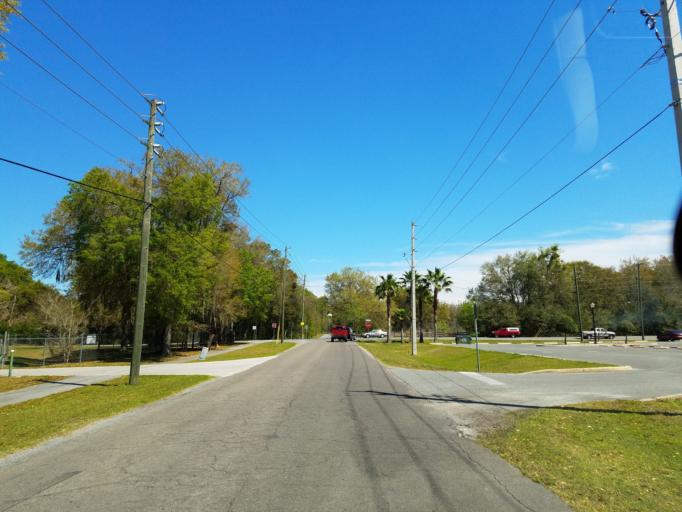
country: US
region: Florida
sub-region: Sumter County
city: Bushnell
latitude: 28.6685
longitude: -82.1053
